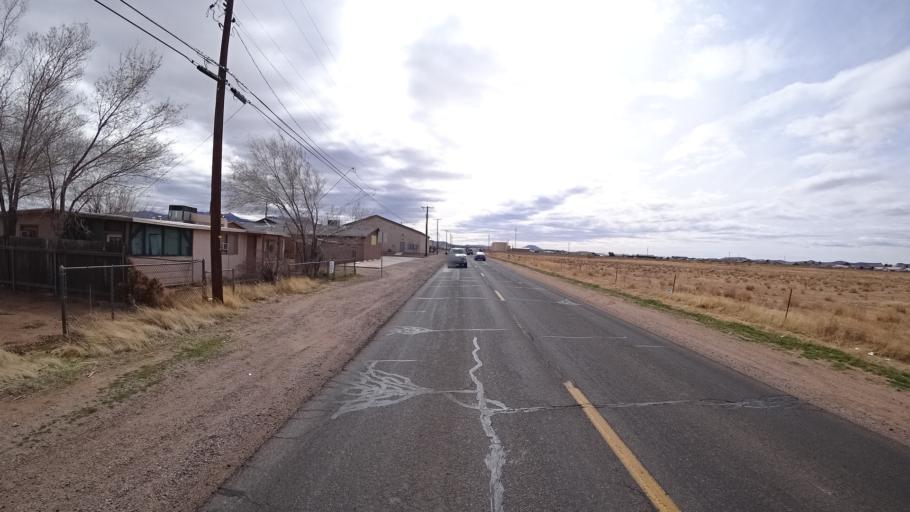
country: US
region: Arizona
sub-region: Mohave County
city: New Kingman-Butler
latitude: 35.2421
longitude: -113.9938
